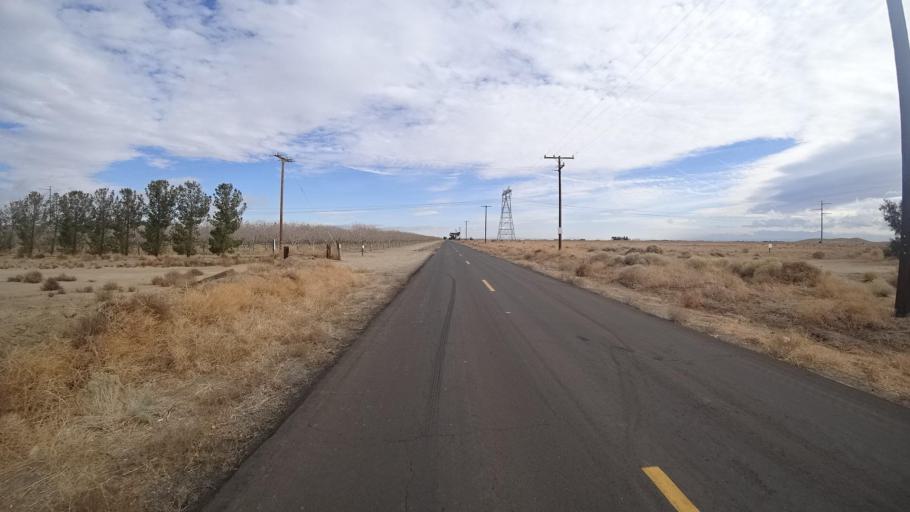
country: US
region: California
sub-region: Kern County
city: Rosamond
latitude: 34.8198
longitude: -118.3221
